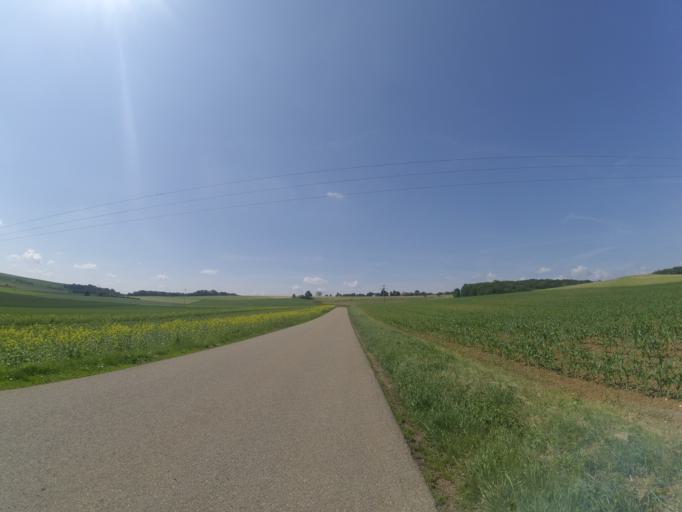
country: DE
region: Baden-Wuerttemberg
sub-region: Tuebingen Region
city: Bernstadt
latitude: 48.4810
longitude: 10.0233
